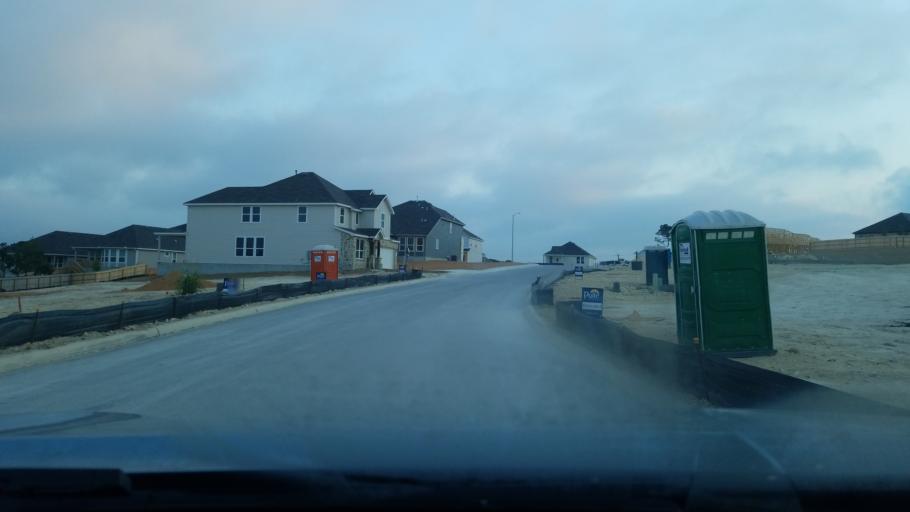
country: US
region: Texas
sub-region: Bexar County
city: Timberwood Park
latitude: 29.7057
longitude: -98.5027
